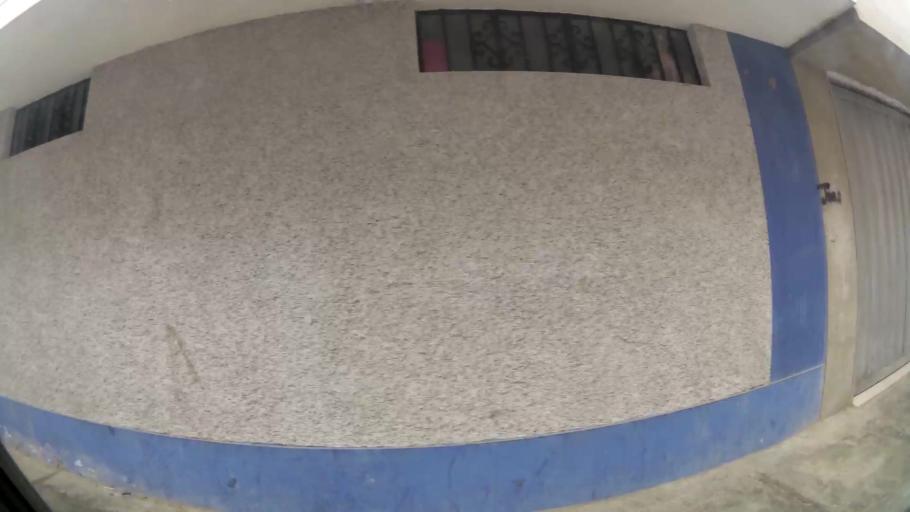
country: PE
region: La Libertad
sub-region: Provincia de Trujillo
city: Trujillo
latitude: -8.1236
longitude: -79.0338
